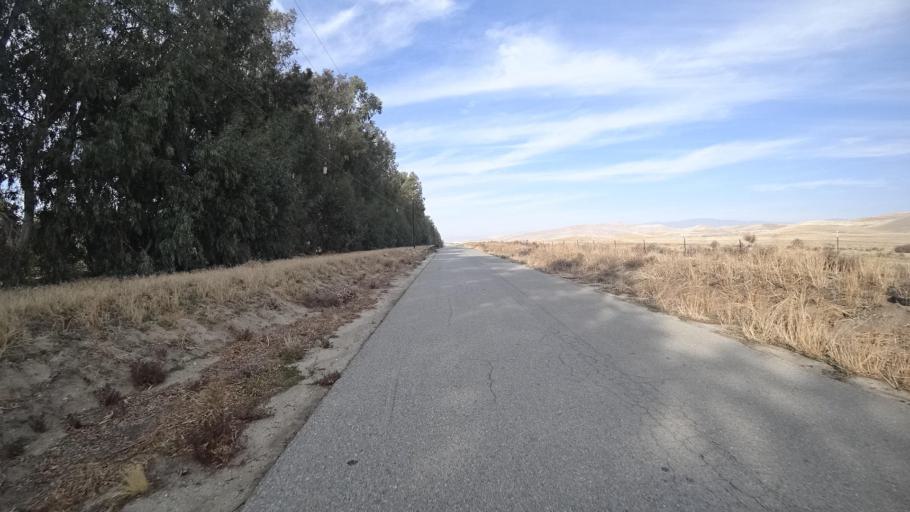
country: US
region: California
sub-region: Kern County
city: Arvin
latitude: 35.2838
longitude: -118.7527
